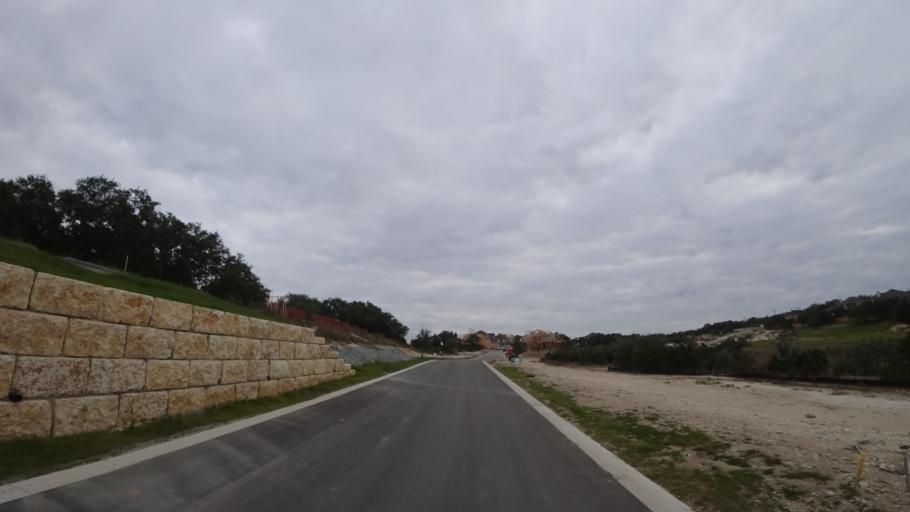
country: US
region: Texas
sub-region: Travis County
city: Bee Cave
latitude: 30.3171
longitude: -97.9132
